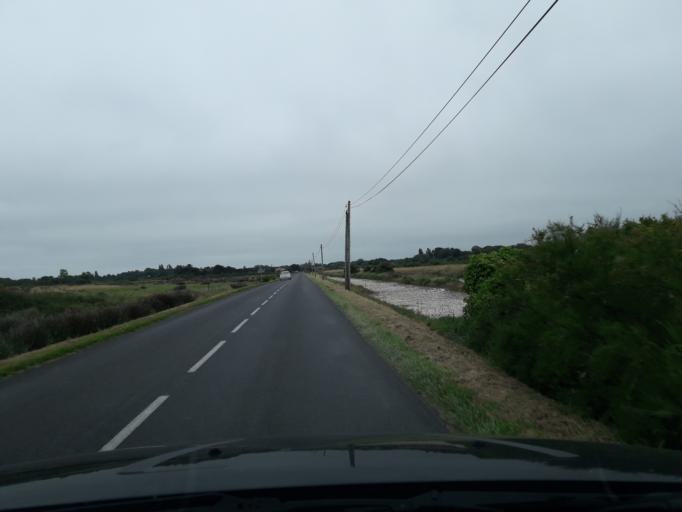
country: FR
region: Poitou-Charentes
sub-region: Departement de la Charente-Maritime
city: Boyard-Ville
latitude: 45.9596
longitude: -1.2491
